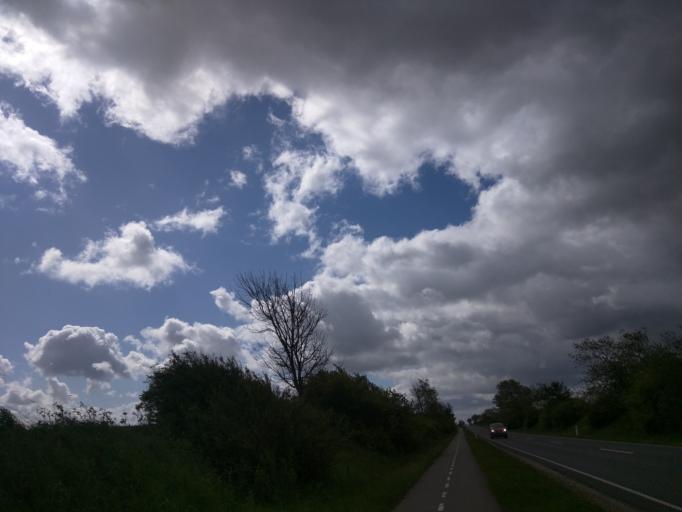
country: DK
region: Central Jutland
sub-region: Silkeborg Kommune
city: Kjellerup
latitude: 56.3145
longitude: 9.4215
